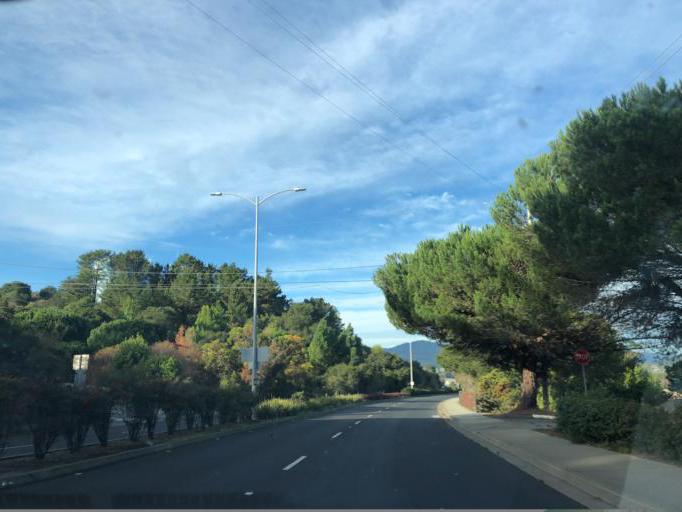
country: US
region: California
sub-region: San Mateo County
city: Highlands-Baywood Park
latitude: 37.5112
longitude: -122.3220
